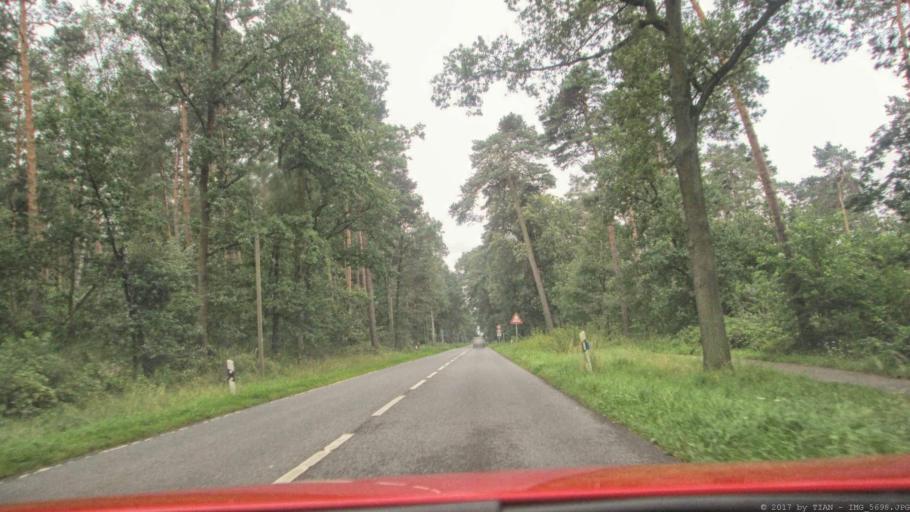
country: DE
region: Lower Saxony
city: Wolfsburg
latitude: 52.4620
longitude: 10.7850
